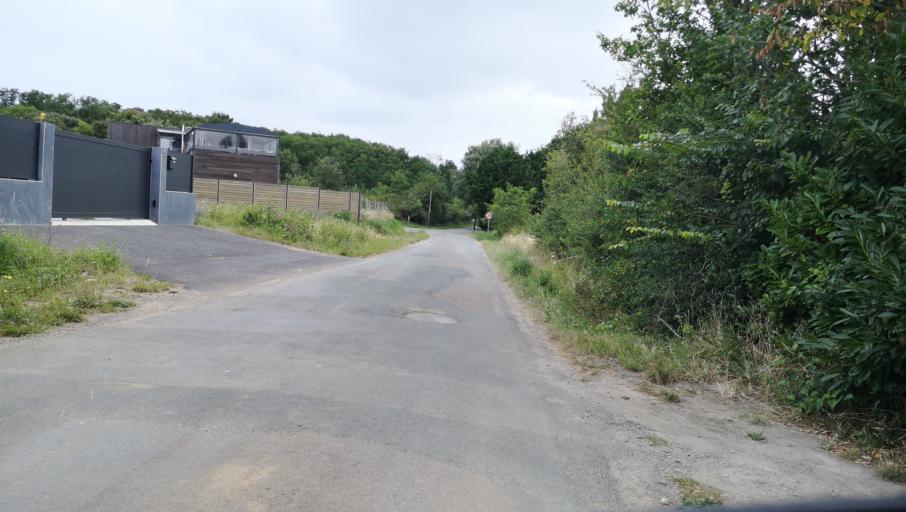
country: FR
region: Pays de la Loire
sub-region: Departement de la Vendee
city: Olonne-sur-Mer
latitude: 46.5570
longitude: -1.8084
